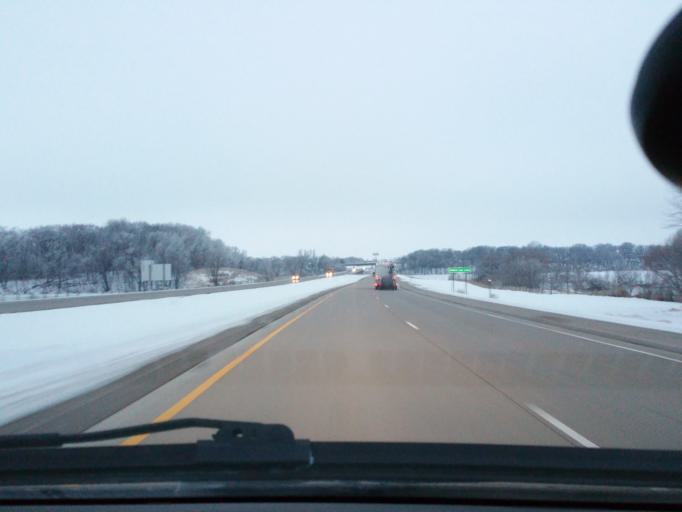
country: US
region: Minnesota
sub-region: Freeborn County
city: Albert Lea
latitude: 43.6330
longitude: -93.3256
